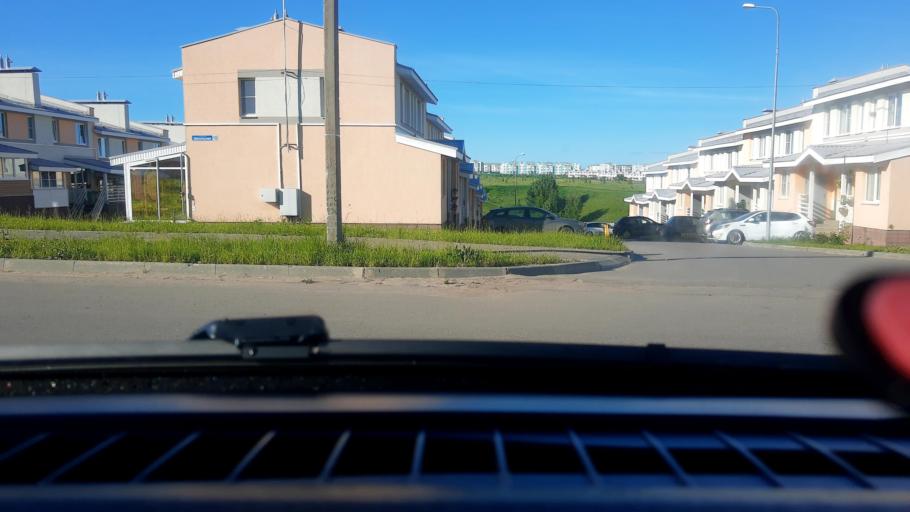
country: RU
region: Nizjnij Novgorod
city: Burevestnik
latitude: 56.1863
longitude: 43.8492
